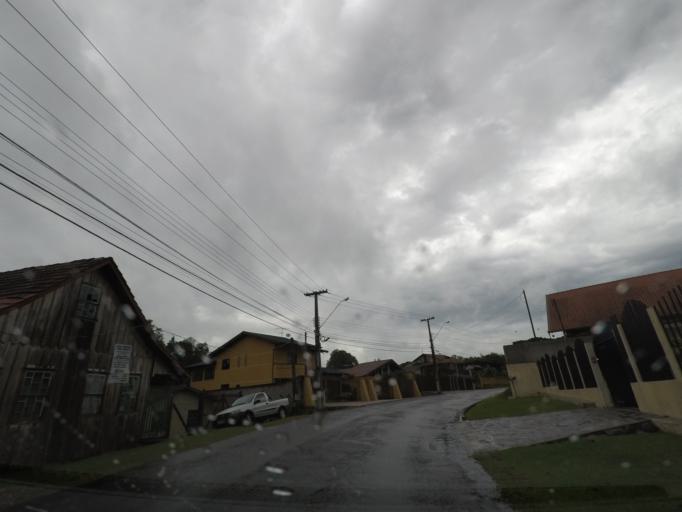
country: BR
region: Parana
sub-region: Campo Largo
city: Campo Largo
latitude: -25.4522
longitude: -49.4520
